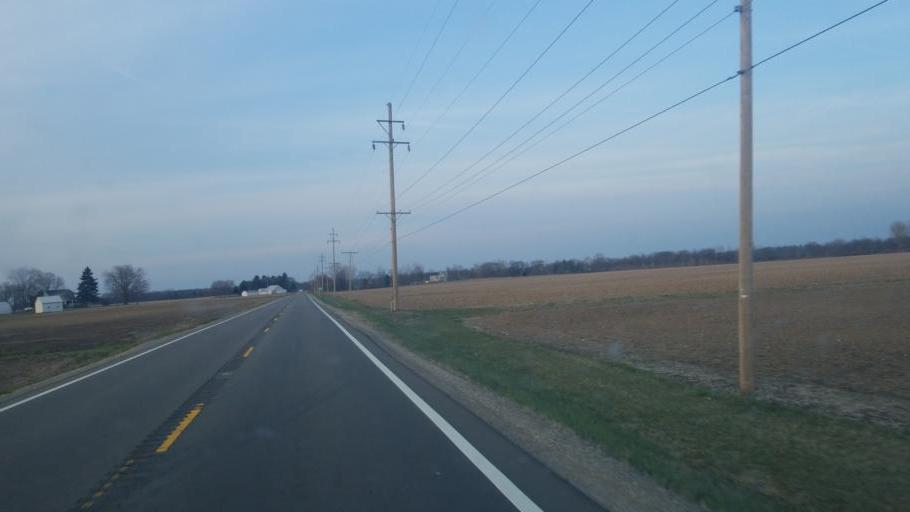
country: US
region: Ohio
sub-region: Marion County
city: Prospect
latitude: 40.4729
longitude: -83.2023
